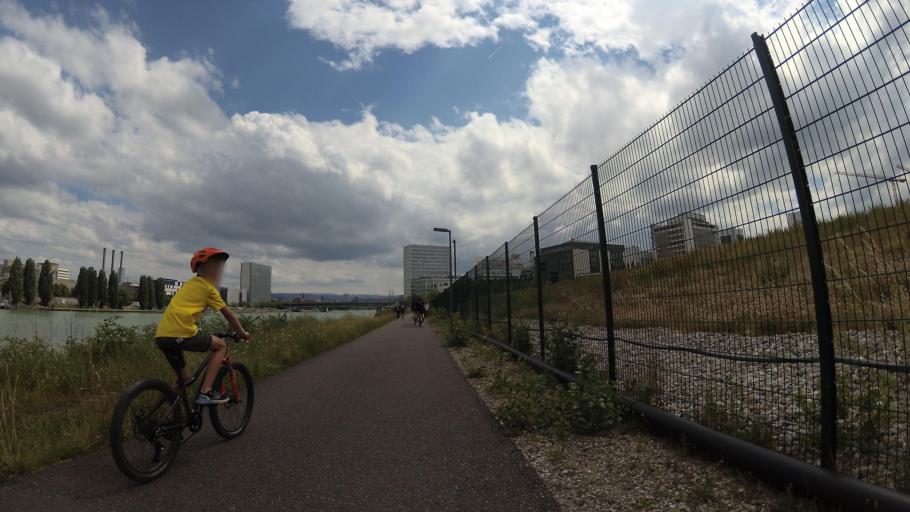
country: FR
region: Alsace
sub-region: Departement du Haut-Rhin
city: Village-Neuf
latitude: 47.5774
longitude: 7.5829
